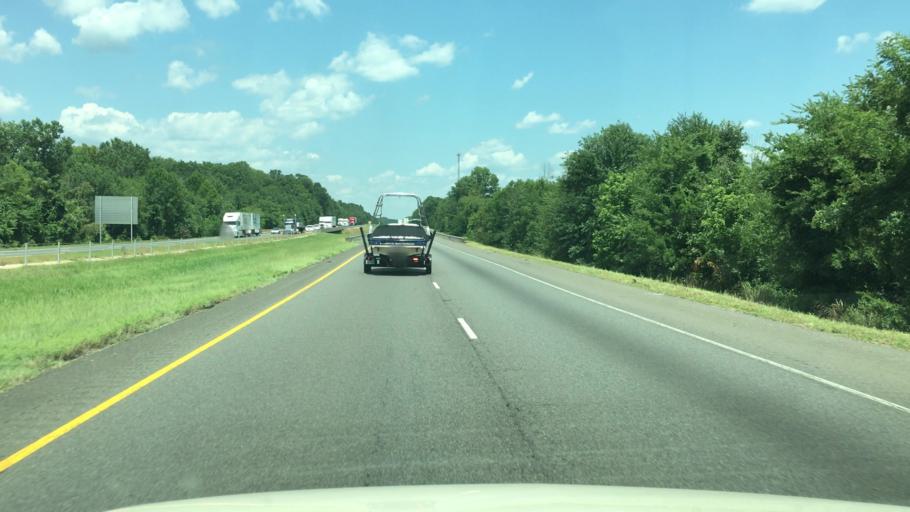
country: US
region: Arkansas
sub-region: Clark County
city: Gurdon
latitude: 34.0119
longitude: -93.1683
